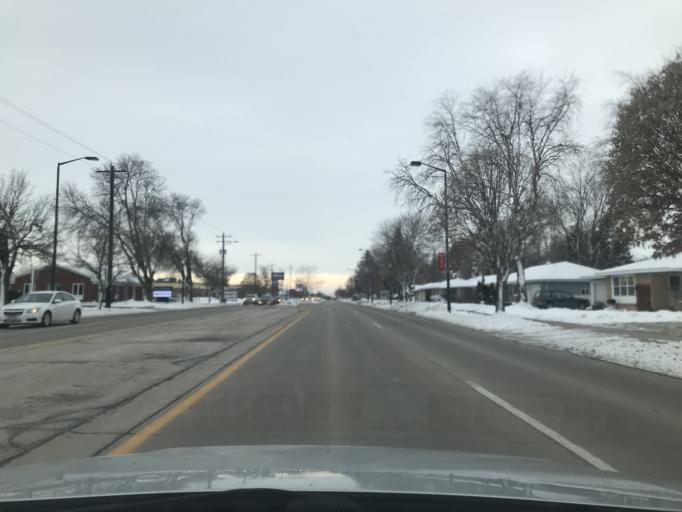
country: US
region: Wisconsin
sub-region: Brown County
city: Ashwaubenon
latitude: 44.4945
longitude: -88.0617
